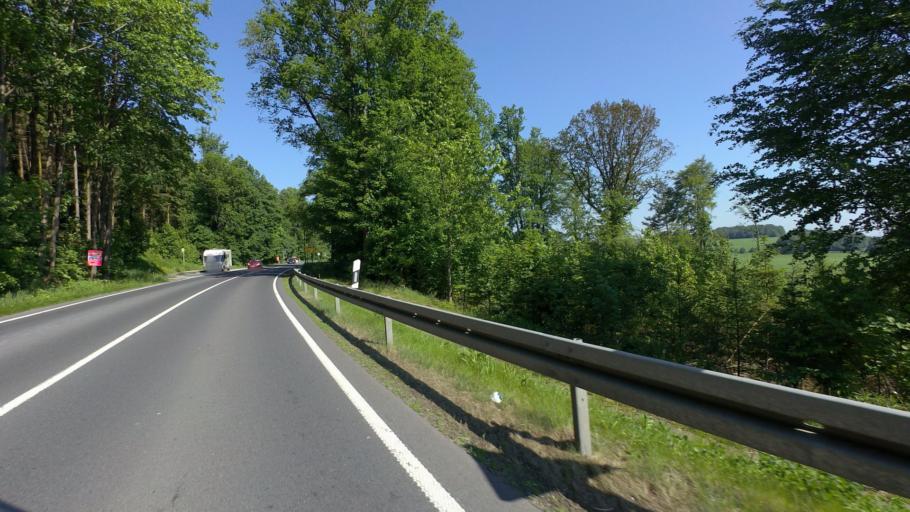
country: DE
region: Saxony
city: Rammenau
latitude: 51.1691
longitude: 14.1420
